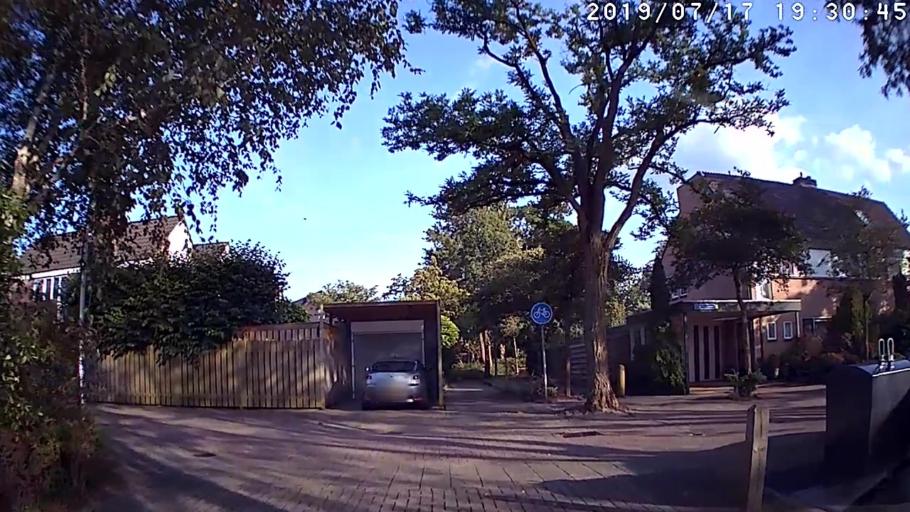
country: NL
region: Overijssel
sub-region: Gemeente Zwolle
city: Zwolle
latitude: 52.5384
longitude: 6.1072
